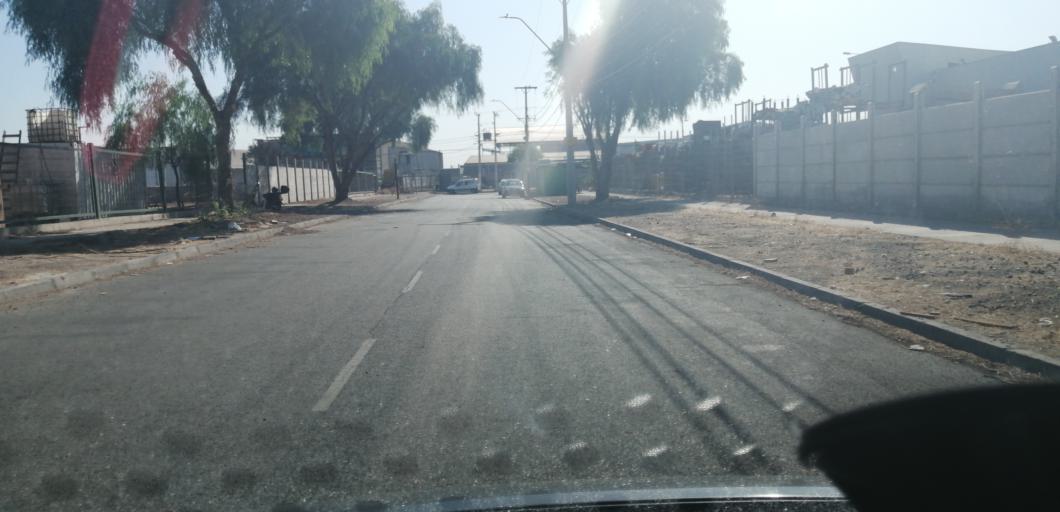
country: CL
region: Santiago Metropolitan
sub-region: Provincia de Santiago
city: Lo Prado
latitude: -33.3827
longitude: -70.7792
